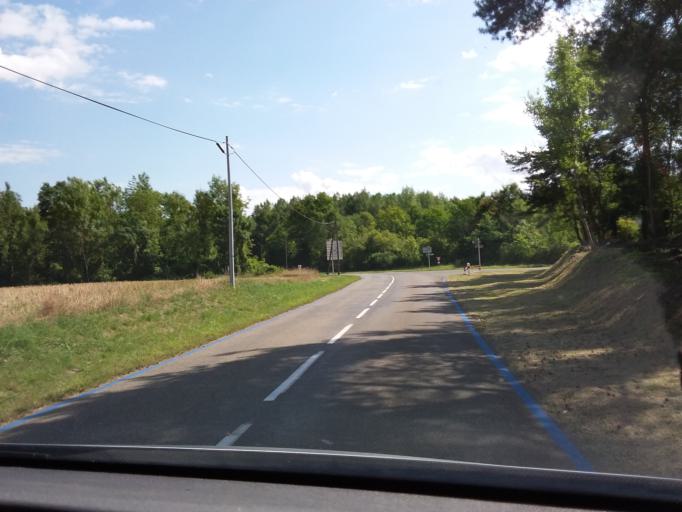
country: FR
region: Picardie
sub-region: Departement de l'Aisne
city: Saint-Erme-Outre-et-Ramecourt
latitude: 49.4487
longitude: 3.8000
